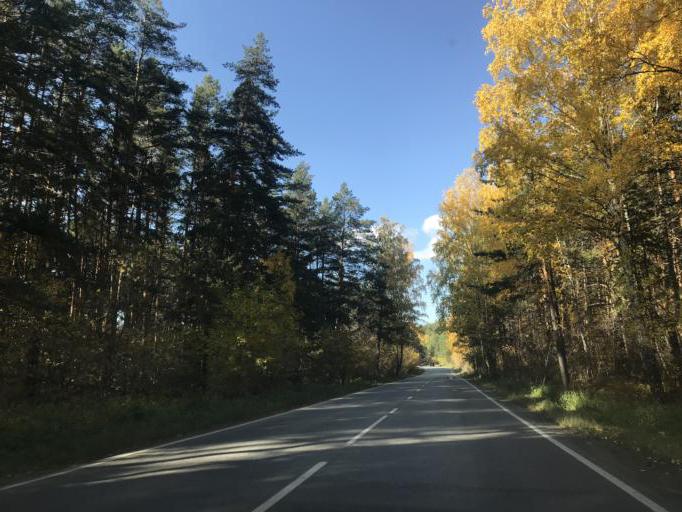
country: RU
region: Chelyabinsk
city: Dolgoderevenskoye
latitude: 55.2852
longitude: 61.3588
